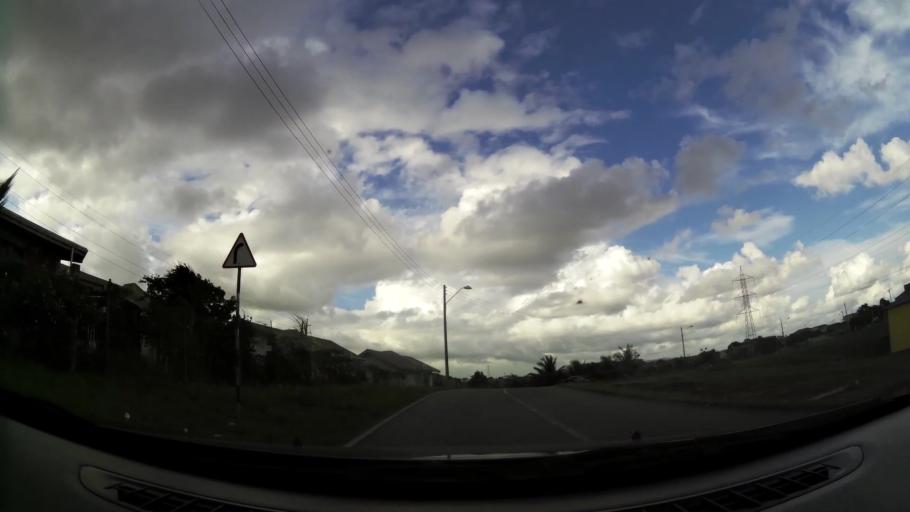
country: TT
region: City of San Fernando
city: Mon Repos
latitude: 10.2695
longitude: -61.4411
